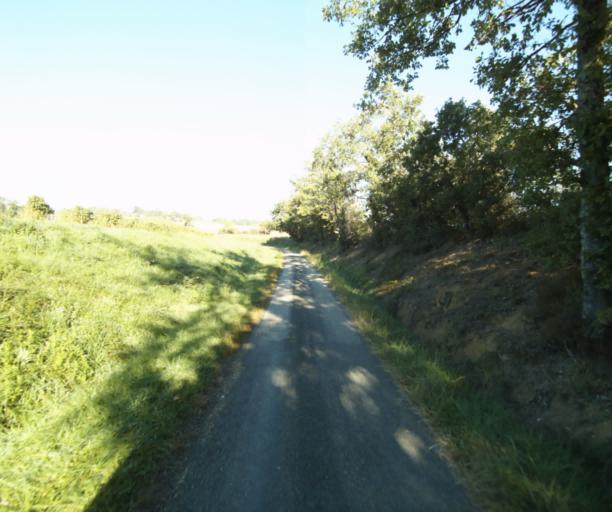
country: FR
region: Midi-Pyrenees
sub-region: Departement du Gers
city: Gondrin
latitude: 43.8406
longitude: 0.2668
